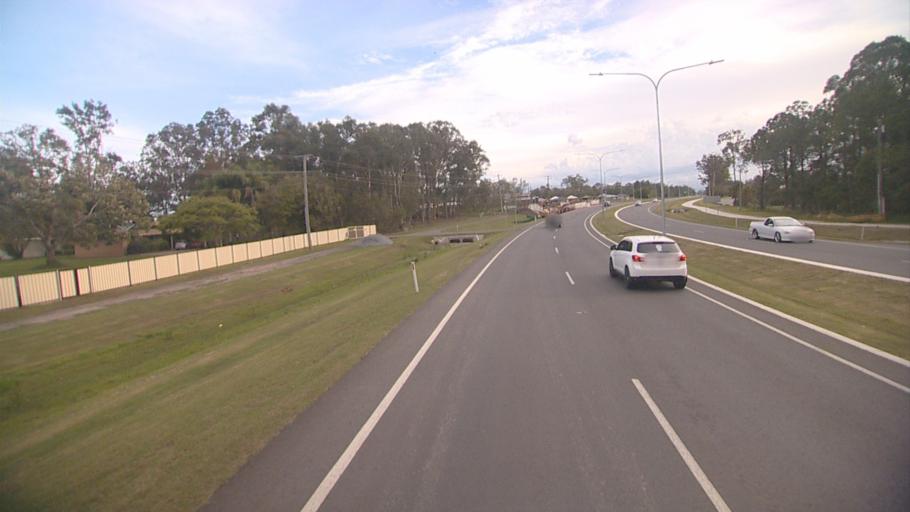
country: AU
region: Queensland
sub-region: Logan
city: Waterford West
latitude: -27.6948
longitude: 153.1025
